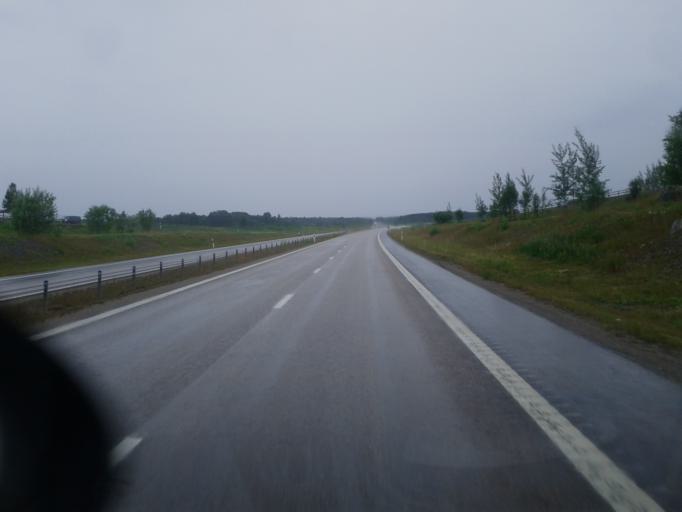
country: SE
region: Uppsala
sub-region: Tierps Kommun
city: Tierp
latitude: 60.3407
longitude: 17.4845
